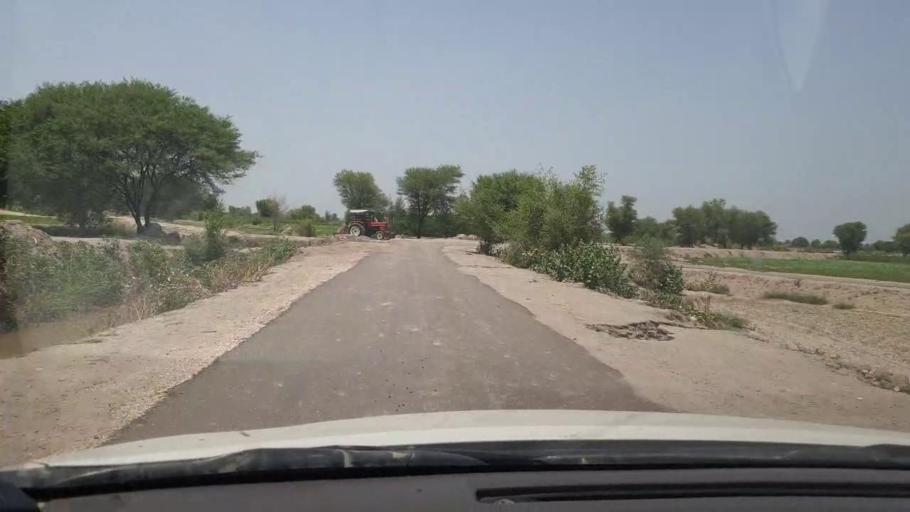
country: PK
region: Sindh
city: Rohri
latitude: 27.5174
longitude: 69.1790
